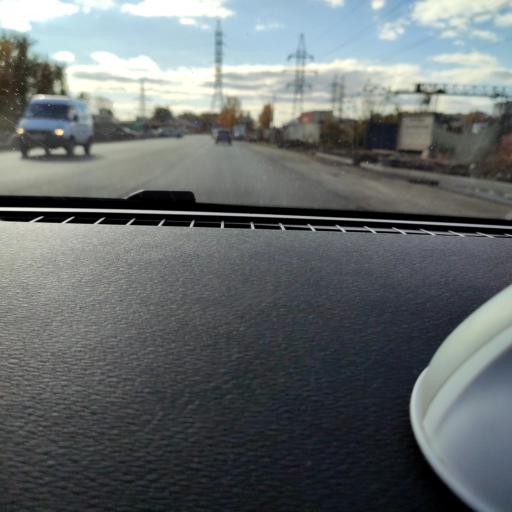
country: RU
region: Samara
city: Samara
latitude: 53.1933
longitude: 50.2304
